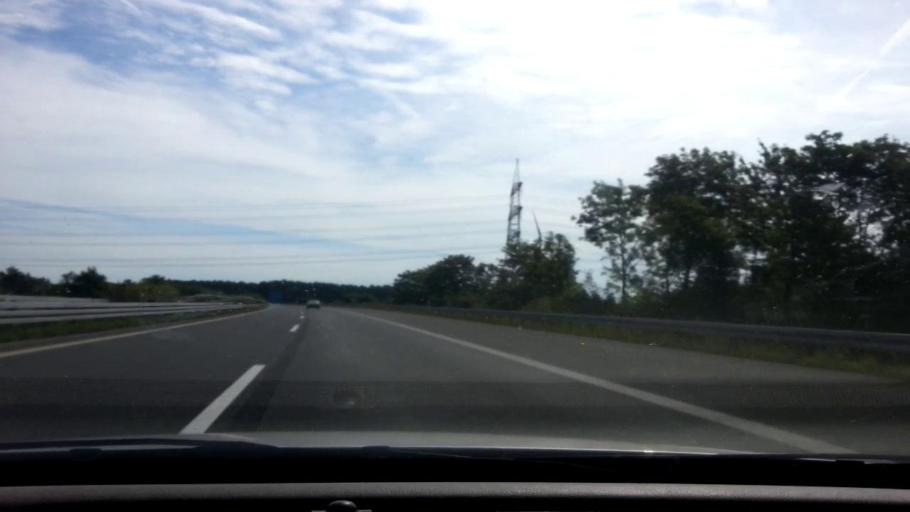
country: DE
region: Bavaria
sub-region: Upper Franconia
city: Wattendorf
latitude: 49.9869
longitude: 11.1073
